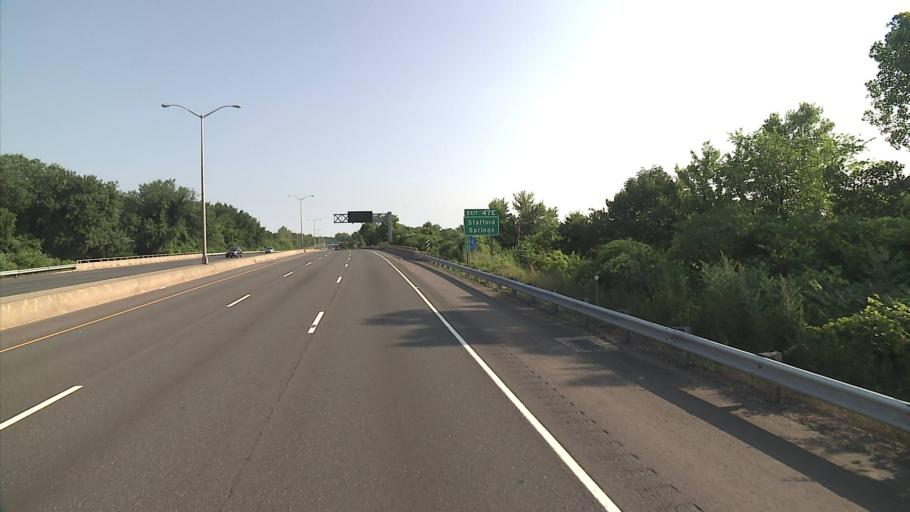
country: US
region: Connecticut
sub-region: Hartford County
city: Enfield
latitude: 41.9756
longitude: -72.5871
